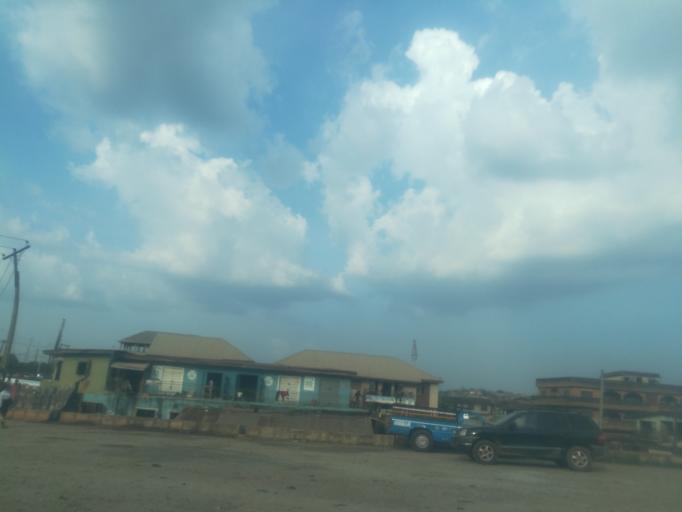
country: NG
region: Ogun
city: Abeokuta
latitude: 7.1506
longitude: 3.3231
